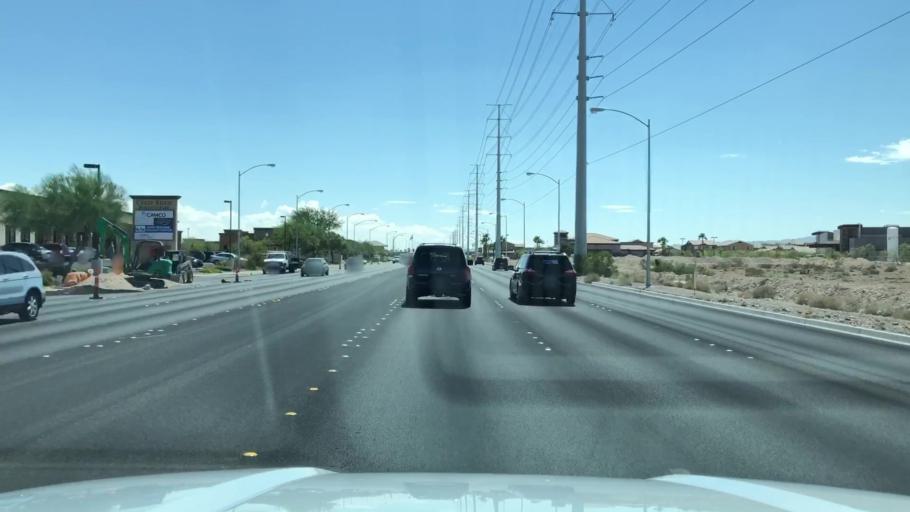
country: US
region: Nevada
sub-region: Clark County
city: Spring Valley
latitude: 36.0810
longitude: -115.2794
